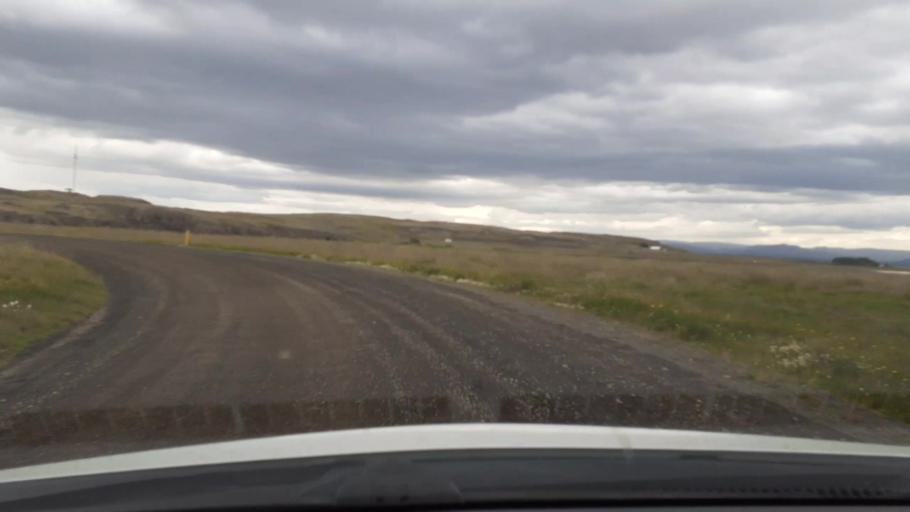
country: IS
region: West
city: Borgarnes
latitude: 64.6029
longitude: -21.6968
